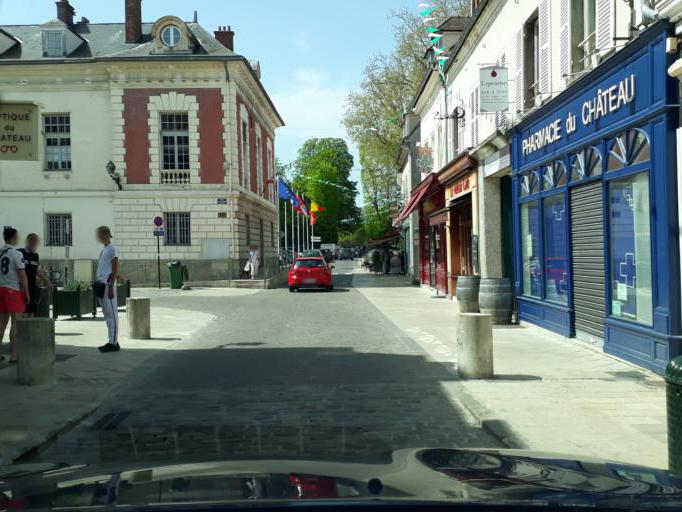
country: FR
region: Ile-de-France
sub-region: Departement des Yvelines
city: Rambouillet
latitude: 48.6453
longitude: 1.8204
